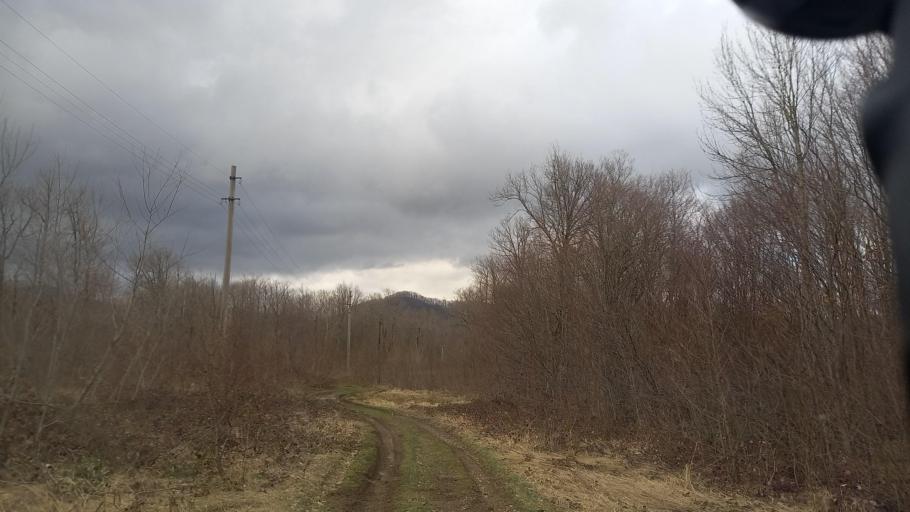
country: RU
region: Krasnodarskiy
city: Dzhubga
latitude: 44.5272
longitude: 38.7732
